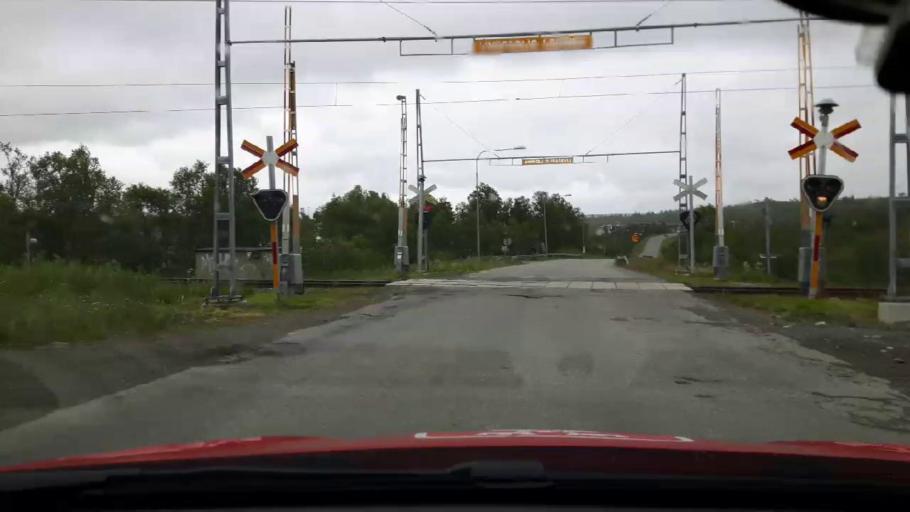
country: NO
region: Nord-Trondelag
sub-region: Meraker
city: Meraker
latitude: 63.3138
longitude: 12.1126
